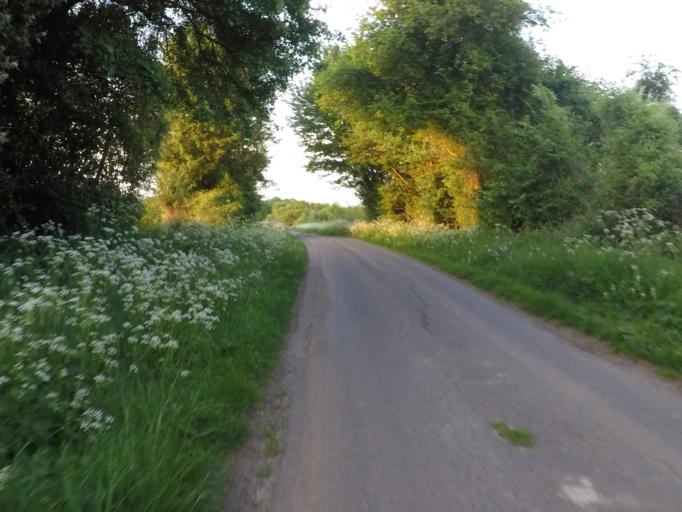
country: GB
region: England
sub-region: Oxfordshire
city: North Leigh
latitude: 51.8253
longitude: -1.4805
